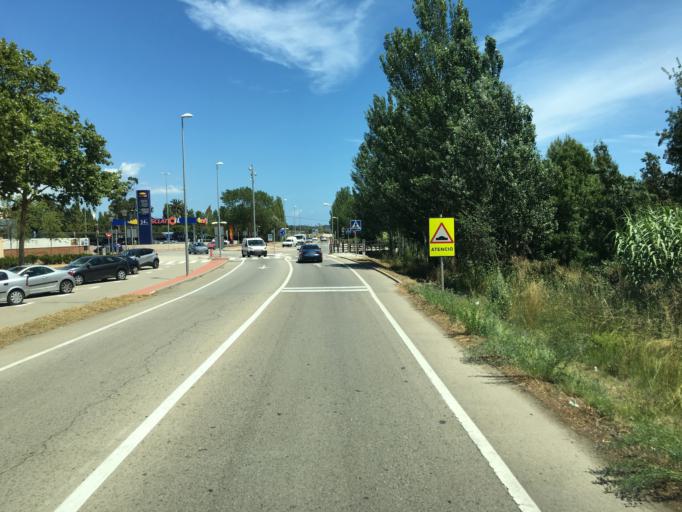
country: ES
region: Catalonia
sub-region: Provincia de Girona
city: Palamos
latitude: 41.8540
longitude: 3.1181
